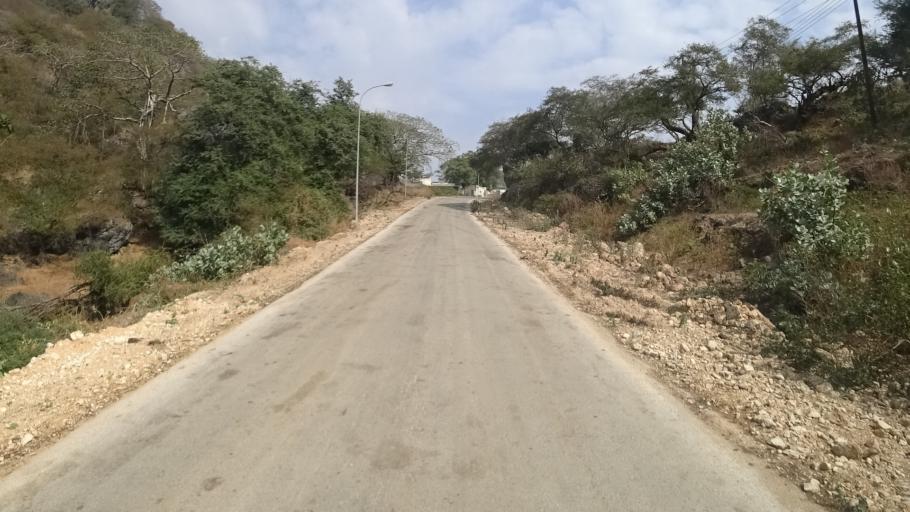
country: YE
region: Al Mahrah
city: Hawf
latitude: 16.7201
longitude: 53.2666
